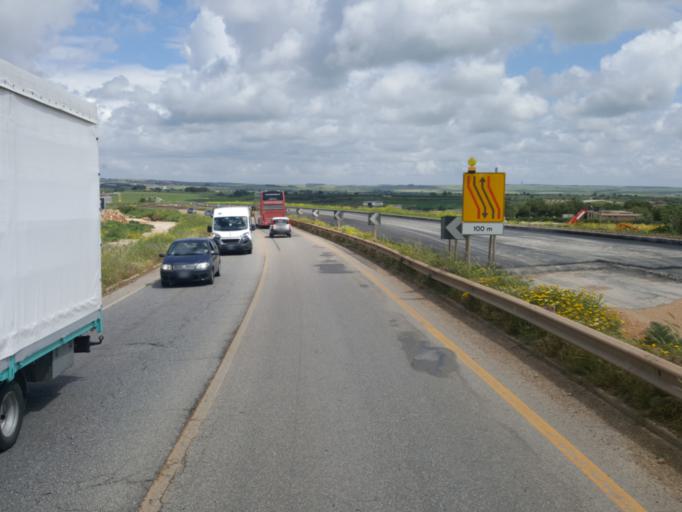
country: IT
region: Apulia
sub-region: Provincia di Bari
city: Altamura
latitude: 40.8177
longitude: 16.5682
